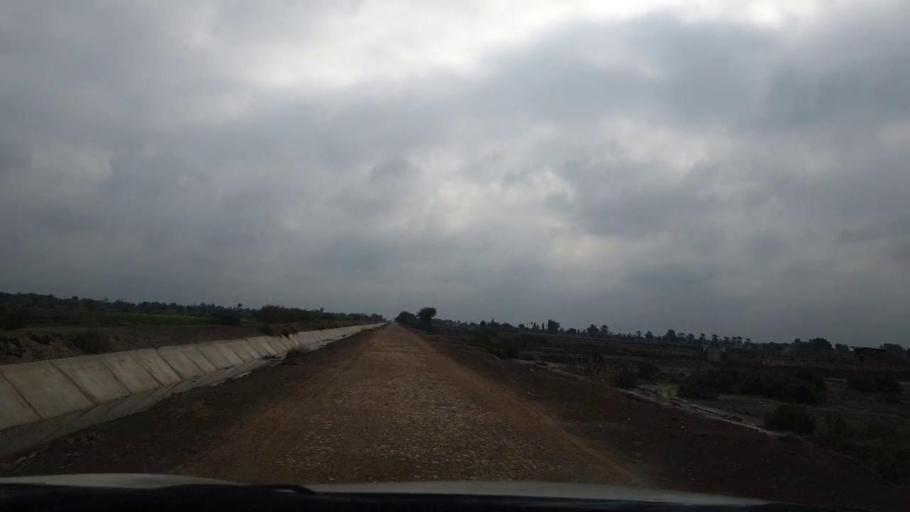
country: PK
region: Sindh
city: Tando Mittha Khan
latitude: 25.8835
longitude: 69.1349
